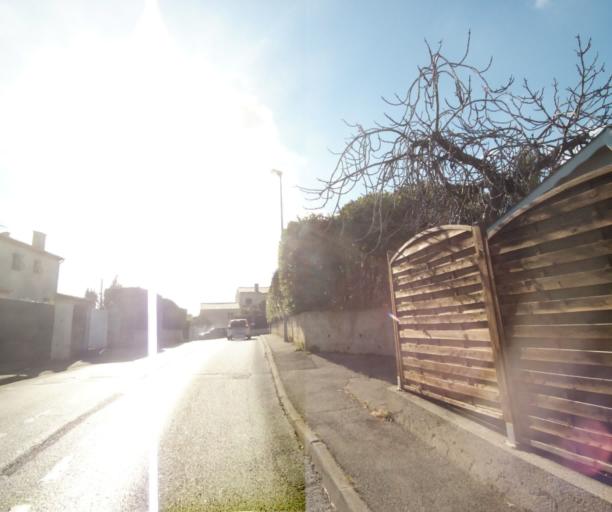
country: FR
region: Provence-Alpes-Cote d'Azur
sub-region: Departement des Alpes-Maritimes
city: Biot
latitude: 43.5997
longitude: 7.1040
